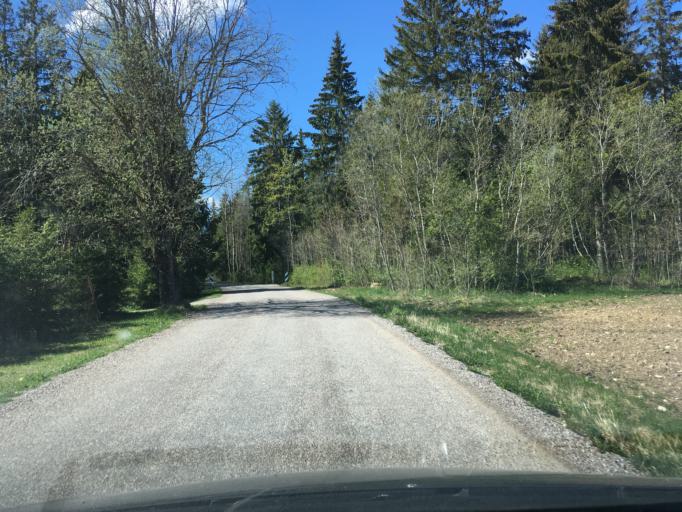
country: EE
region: Harju
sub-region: Rae vald
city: Vaida
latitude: 59.2004
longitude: 25.0809
